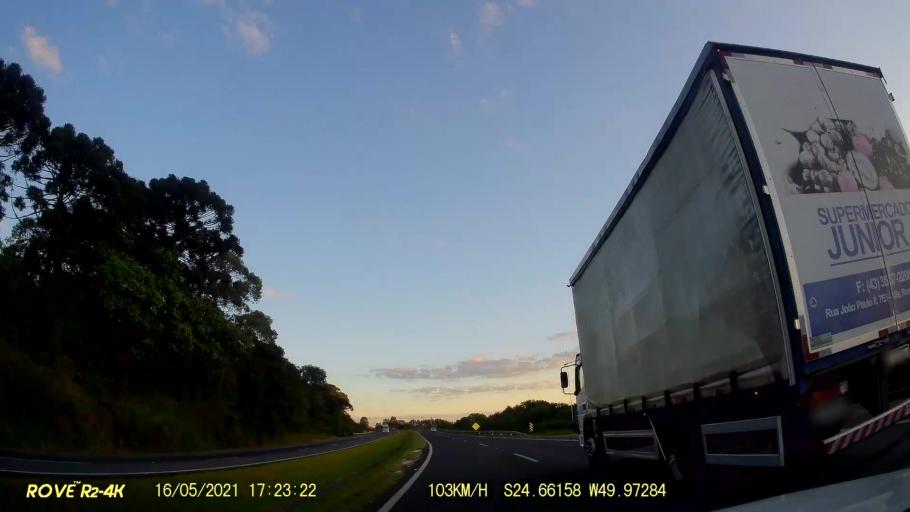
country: BR
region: Parana
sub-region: Castro
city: Castro
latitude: -24.6616
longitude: -49.9730
